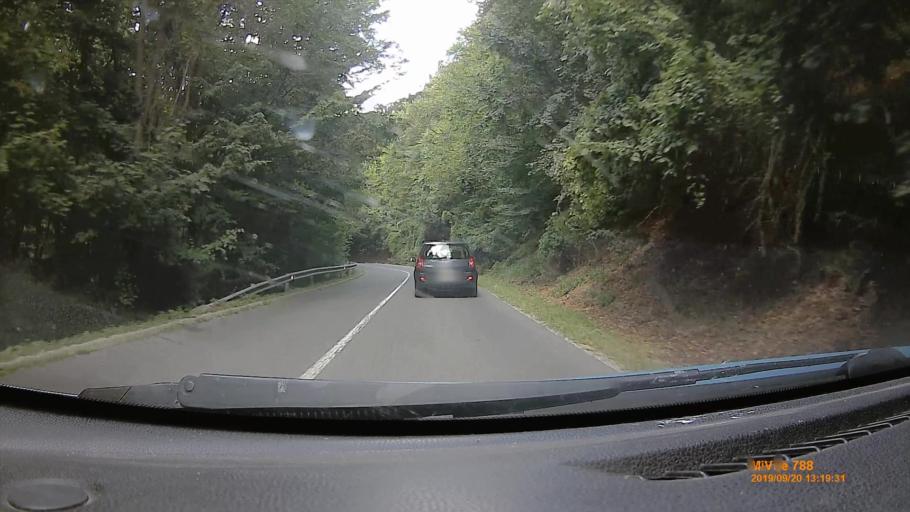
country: HU
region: Heves
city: Felsotarkany
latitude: 48.0080
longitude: 20.4654
